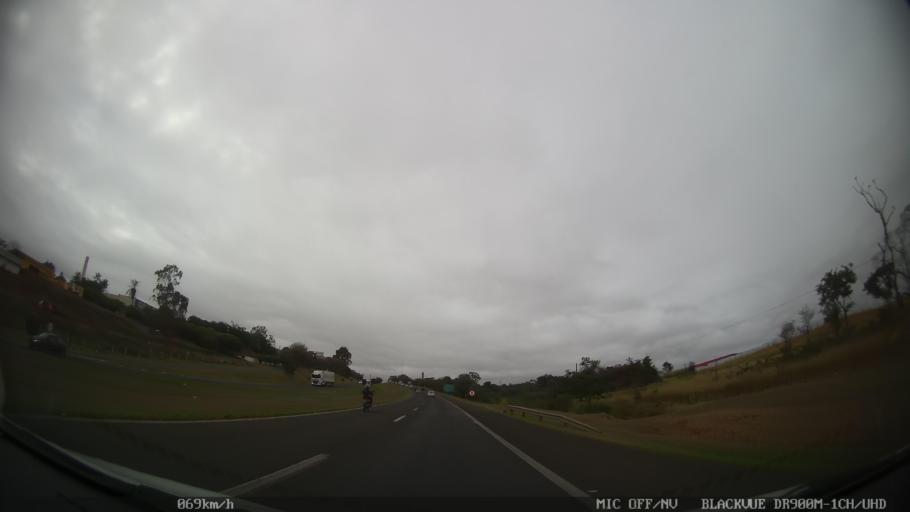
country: BR
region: Sao Paulo
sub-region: Sao Jose Do Rio Preto
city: Sao Jose do Rio Preto
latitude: -20.8212
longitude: -49.4288
